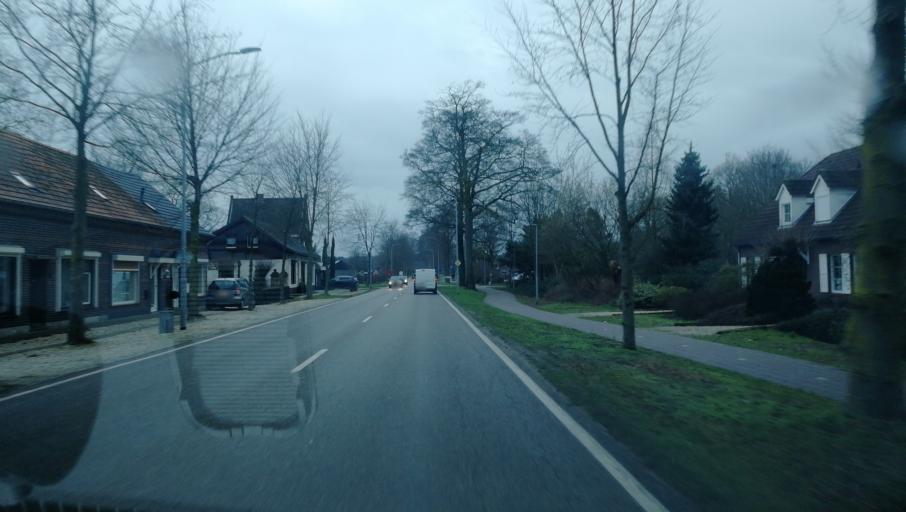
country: NL
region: Limburg
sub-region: Gemeente Venlo
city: Tegelen
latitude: 51.3556
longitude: 6.1282
